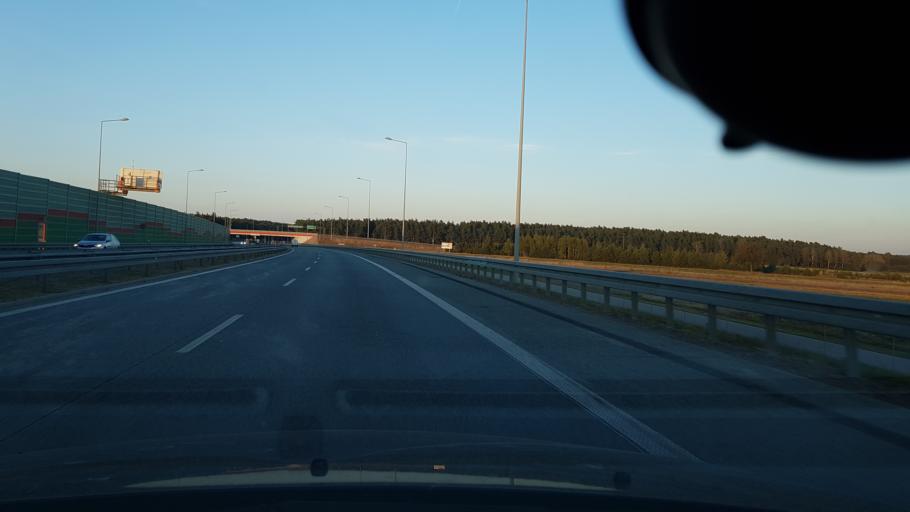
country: PL
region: Lodz Voivodeship
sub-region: Powiat tomaszowski
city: Lubochnia
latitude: 51.6206
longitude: 20.0925
